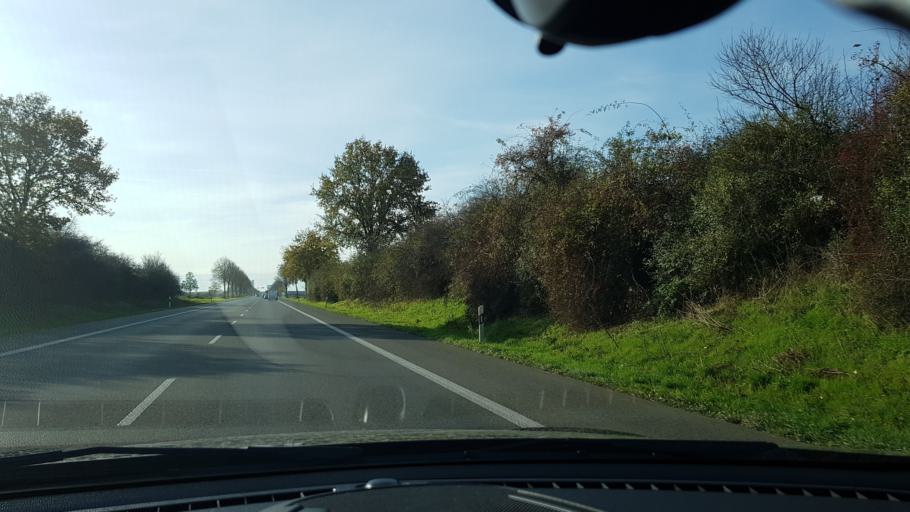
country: DE
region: North Rhine-Westphalia
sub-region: Regierungsbezirk Dusseldorf
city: Grevenbroich
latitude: 51.0976
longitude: 6.6208
